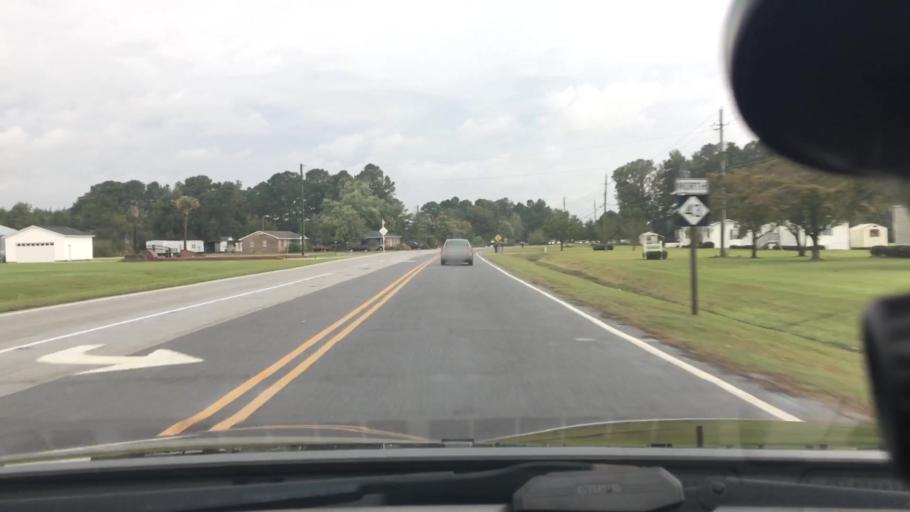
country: US
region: North Carolina
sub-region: Pitt County
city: Windsor
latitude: 35.5130
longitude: -77.3188
